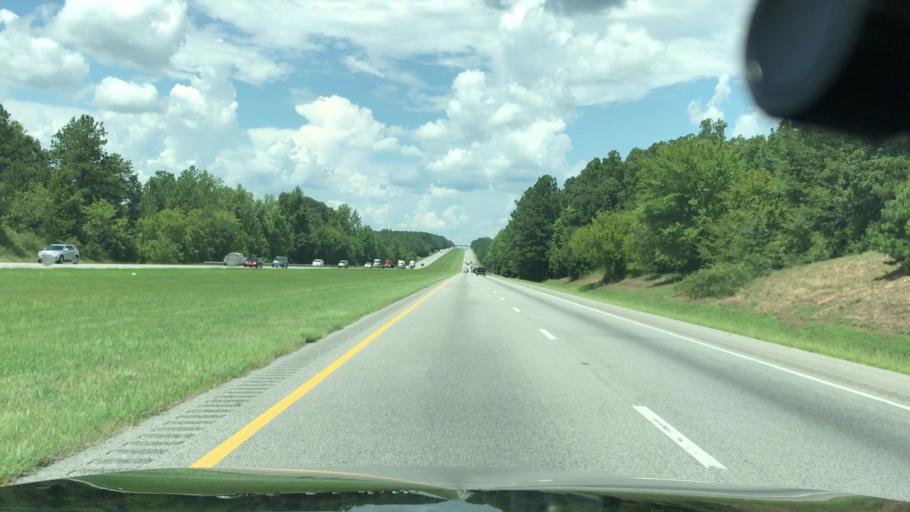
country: US
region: South Carolina
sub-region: Chester County
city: Great Falls
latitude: 34.6581
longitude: -81.0288
